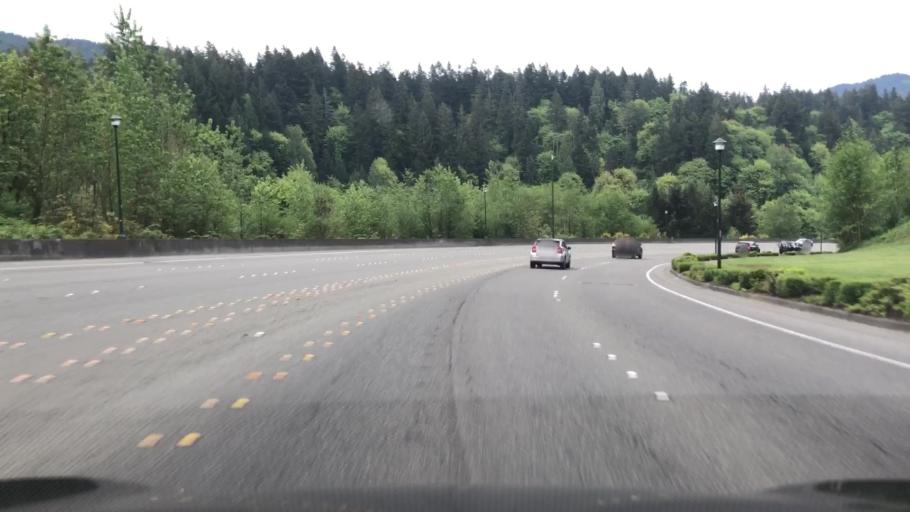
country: US
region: Washington
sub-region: King County
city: Issaquah
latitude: 47.5360
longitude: -122.0174
